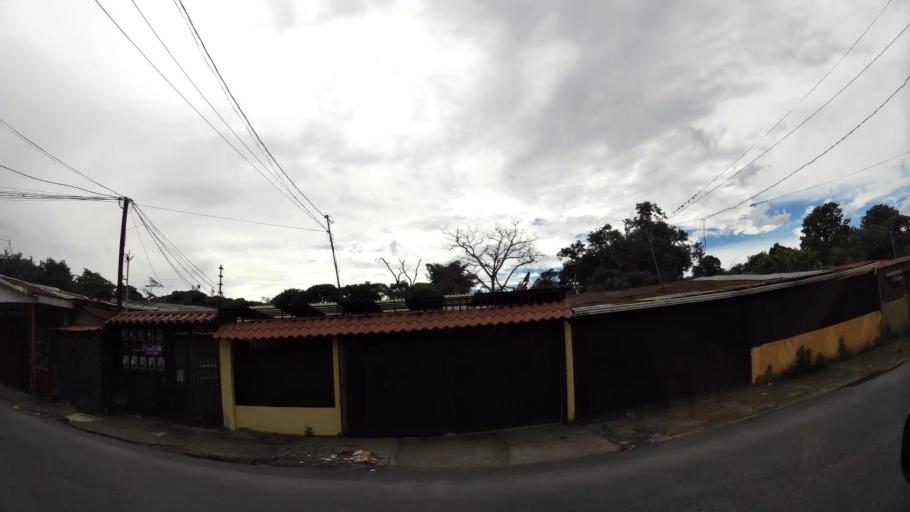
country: CR
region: San Jose
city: Purral
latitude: 9.9556
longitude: -84.0340
